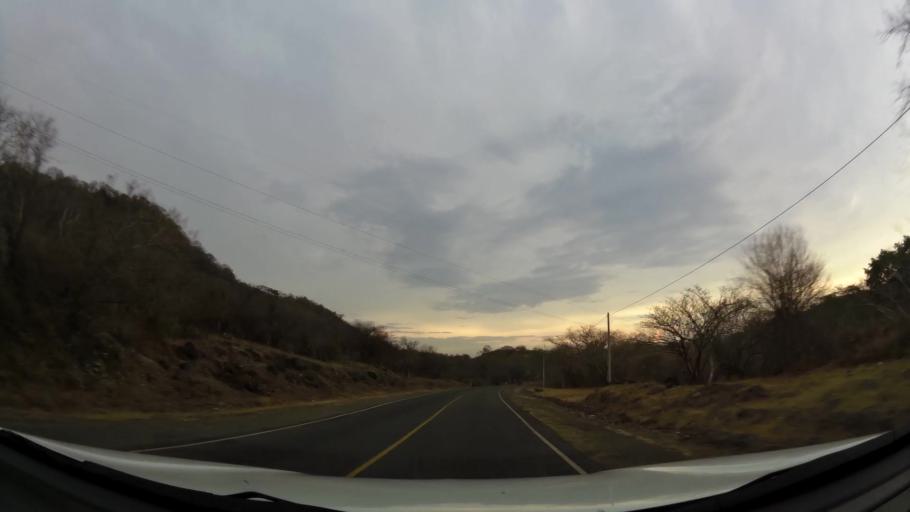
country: NI
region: Leon
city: La Jicaral
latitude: 12.6926
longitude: -86.4086
